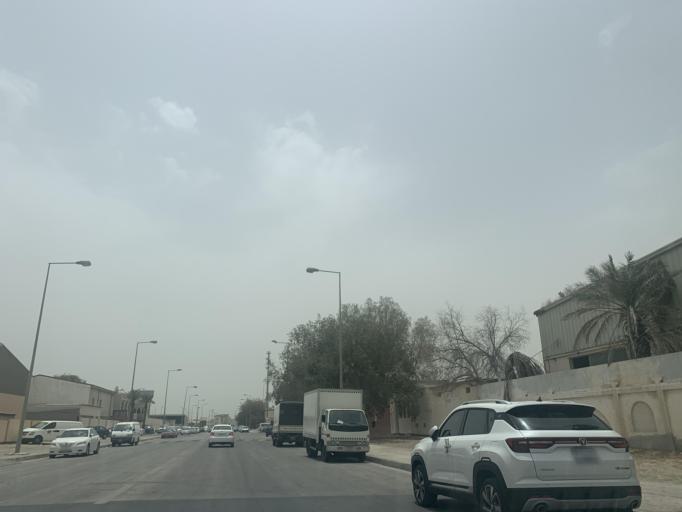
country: BH
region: Northern
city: Sitrah
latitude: 26.1819
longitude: 50.6098
